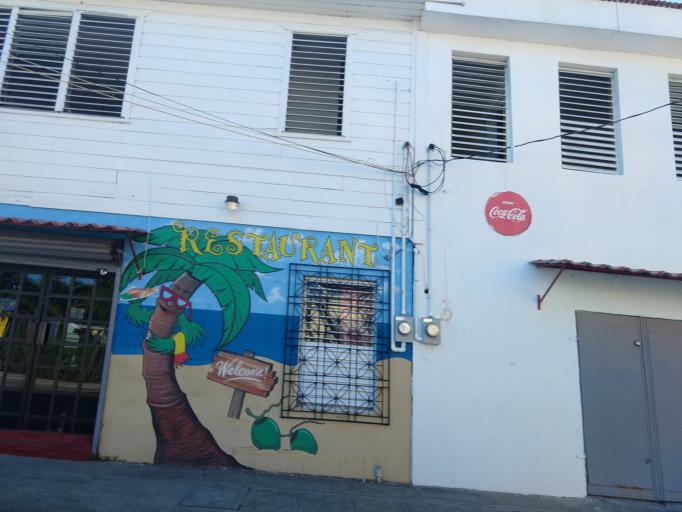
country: BZ
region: Belize
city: Belize City
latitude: 17.5002
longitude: -88.1863
